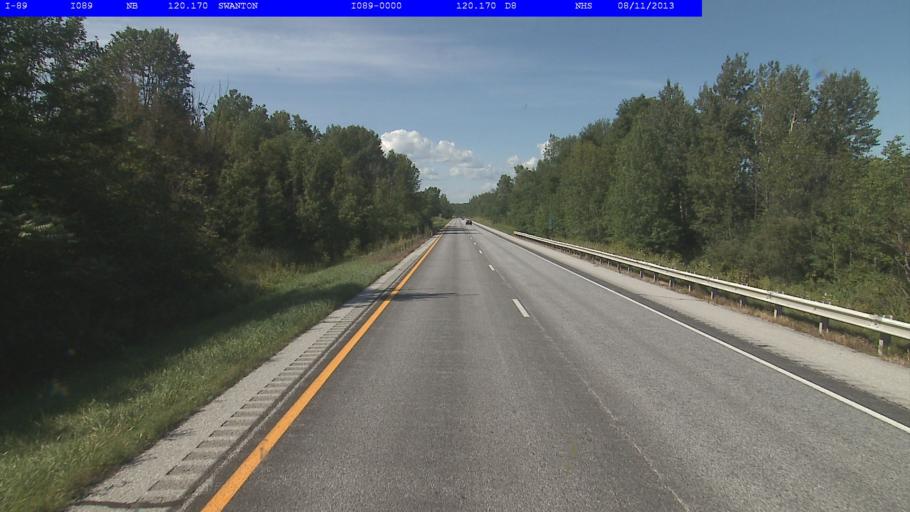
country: US
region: Vermont
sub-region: Franklin County
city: Swanton
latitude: 44.8795
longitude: -73.0836
